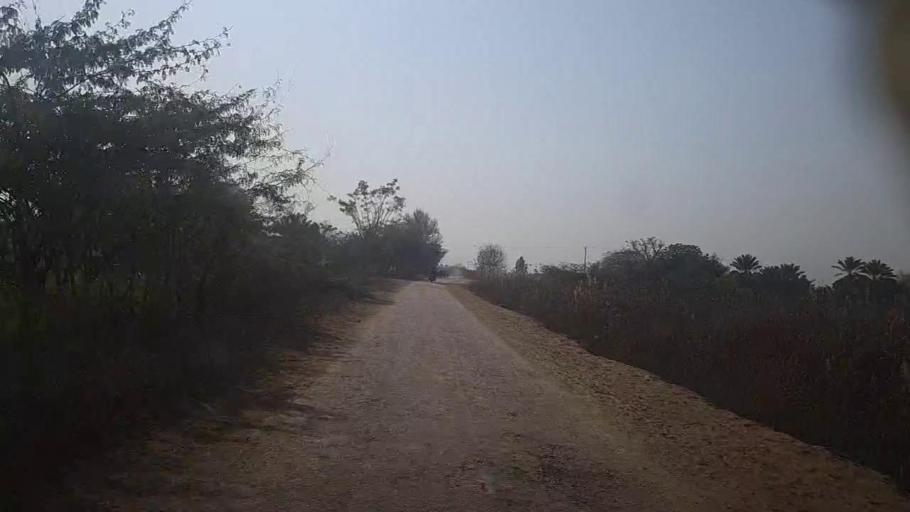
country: PK
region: Sindh
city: Kot Diji
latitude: 27.4132
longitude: 68.7937
